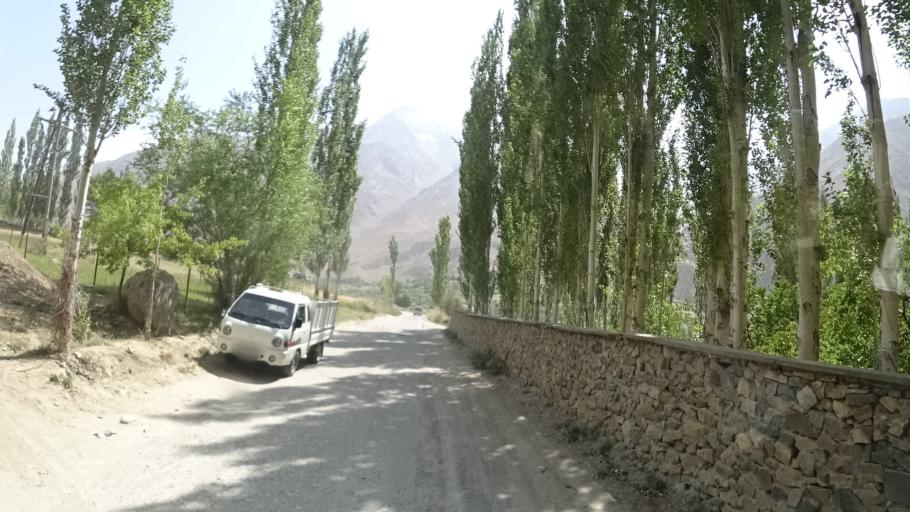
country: TJ
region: Gorno-Badakhshan
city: Ishqoshim
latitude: 36.9261
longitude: 71.4934
